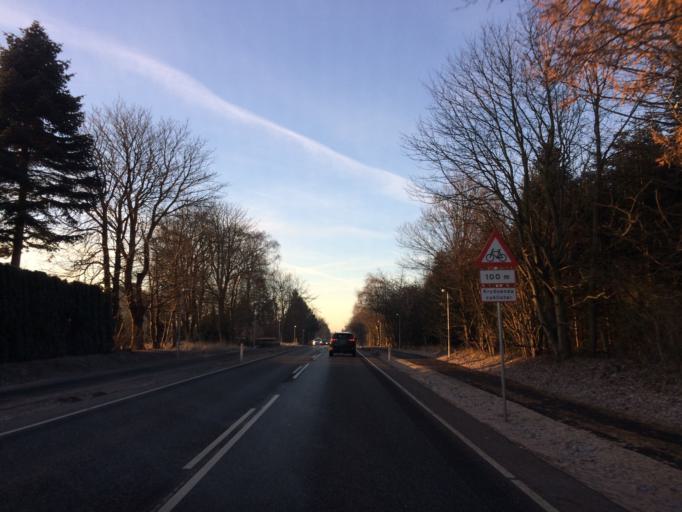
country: DK
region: South Denmark
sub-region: Odense Kommune
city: Bellinge
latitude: 55.3270
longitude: 10.3256
